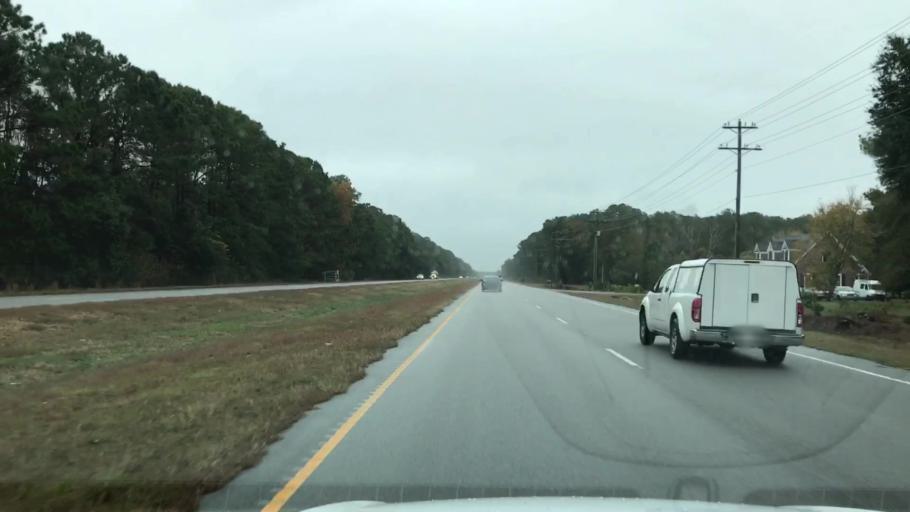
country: US
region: South Carolina
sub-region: Charleston County
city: Isle of Palms
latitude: 32.9008
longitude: -79.7307
